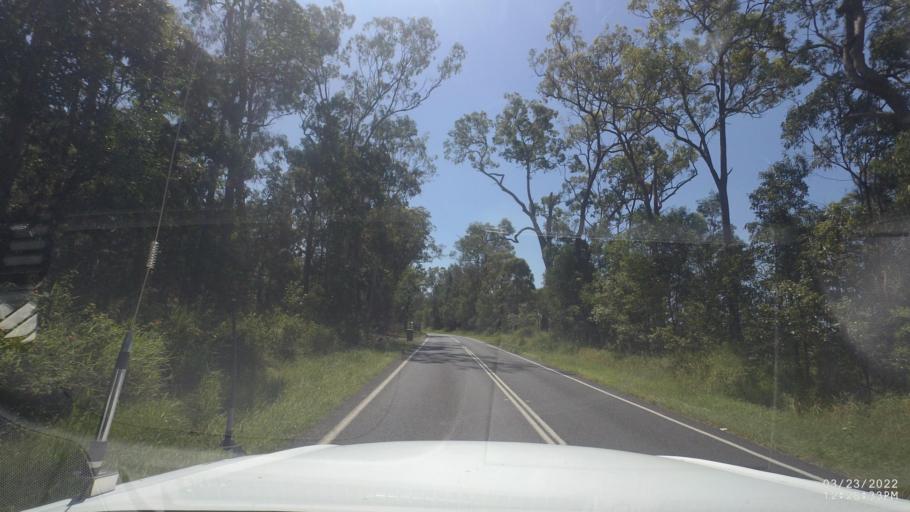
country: AU
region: Queensland
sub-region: Logan
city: Chambers Flat
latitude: -27.8142
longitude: 153.0974
